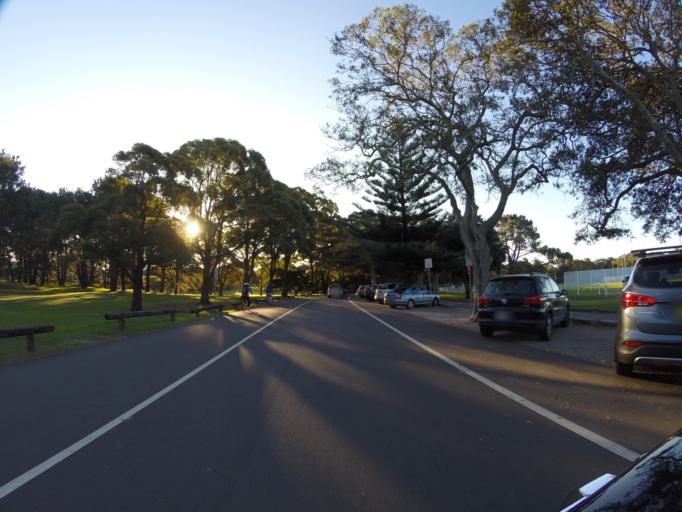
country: AU
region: New South Wales
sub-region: Woollahra
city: Woollahra
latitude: -33.9011
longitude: 151.2283
